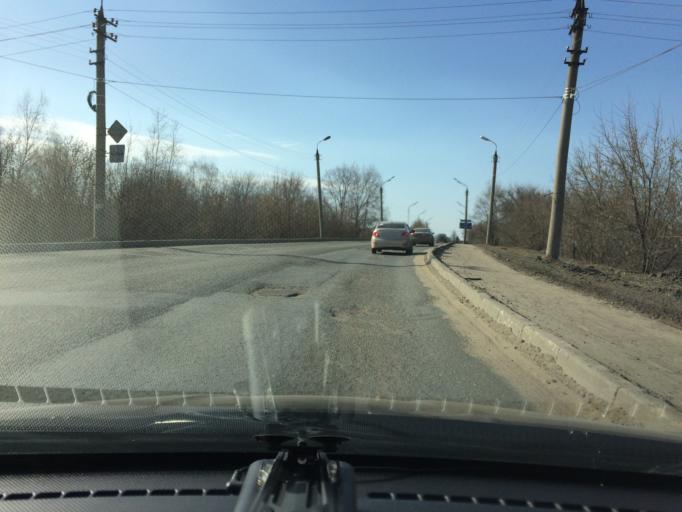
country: RU
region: Mariy-El
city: Yoshkar-Ola
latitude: 56.6434
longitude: 47.9134
